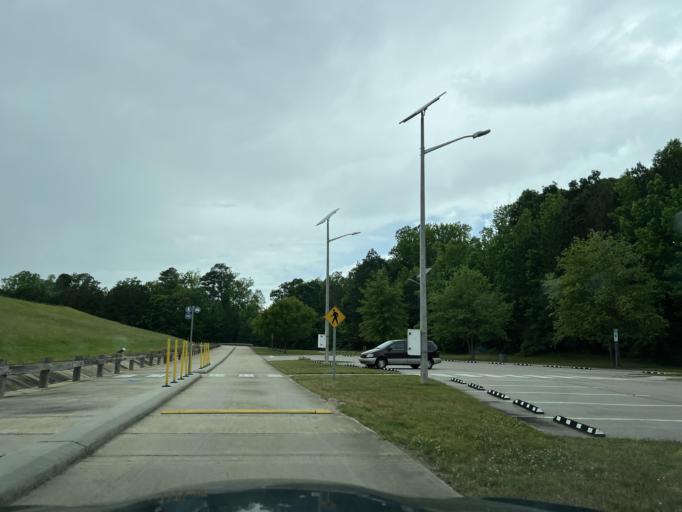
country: US
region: North Carolina
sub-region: Wake County
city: Wake Forest
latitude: 35.9099
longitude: -78.5794
